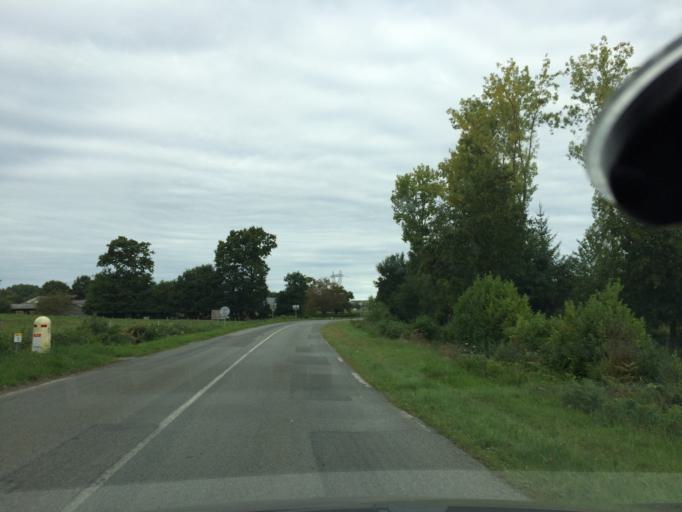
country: FR
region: Brittany
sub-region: Departement d'Ille-et-Vilaine
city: Hede-Bazouges
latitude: 48.2973
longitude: -1.8093
